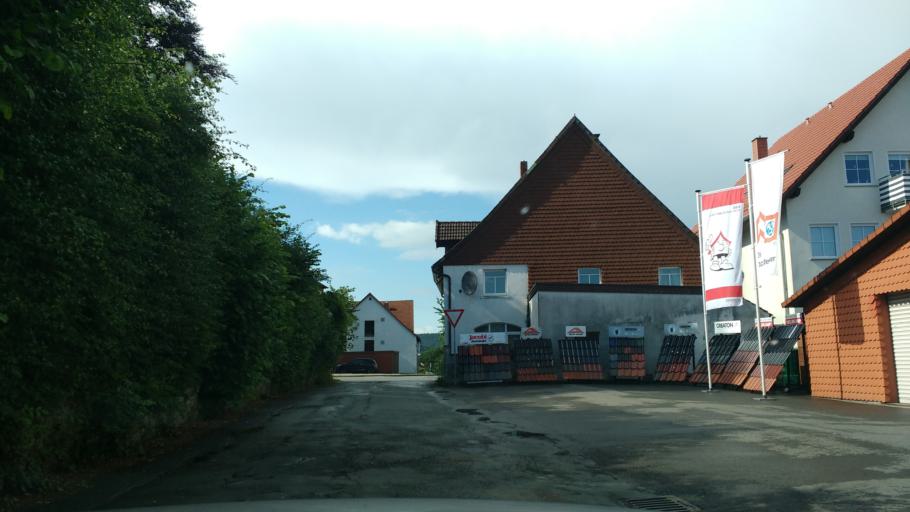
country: DE
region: North Rhine-Westphalia
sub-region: Regierungsbezirk Detmold
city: Barntrup
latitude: 52.0316
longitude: 9.1213
